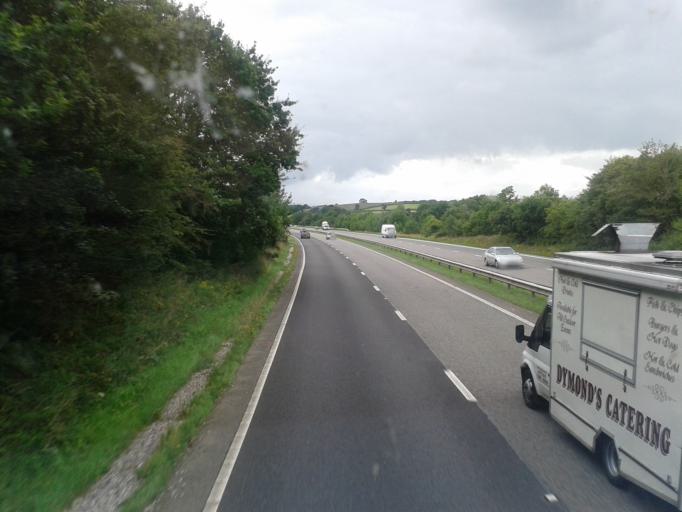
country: GB
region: England
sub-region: Devon
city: Crediton
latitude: 50.7304
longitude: -3.6839
